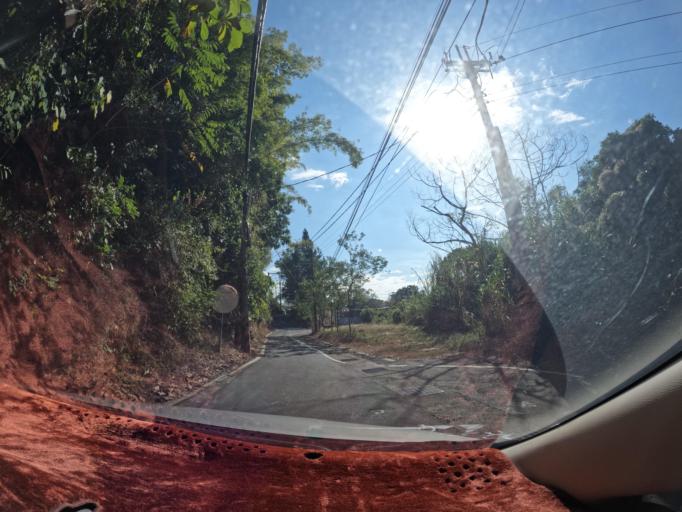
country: TW
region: Taiwan
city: Yujing
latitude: 23.0276
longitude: 120.3854
